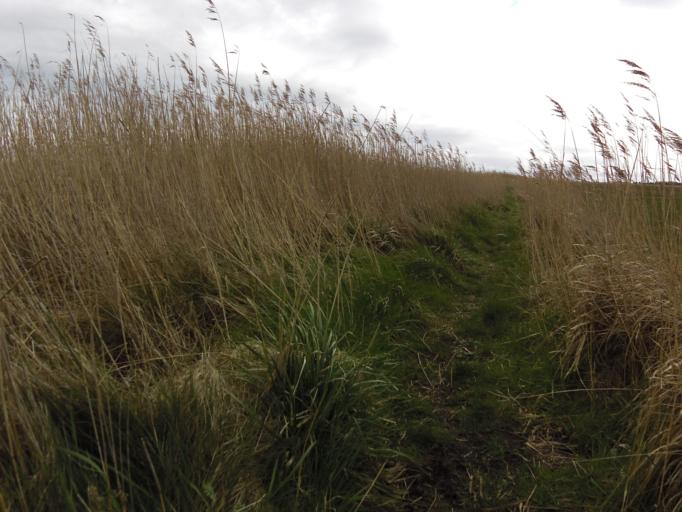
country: DE
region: Mecklenburg-Vorpommern
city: Hiddensee
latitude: 54.5545
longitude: 13.1156
